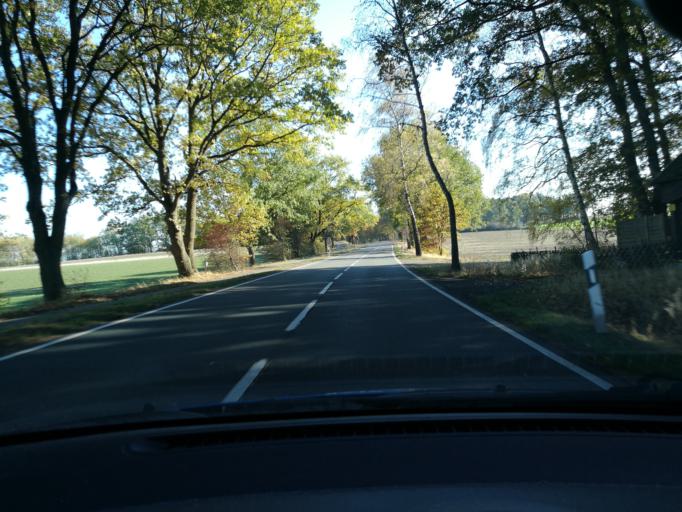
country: DE
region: Lower Saxony
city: Karwitz
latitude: 53.1044
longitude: 11.0468
